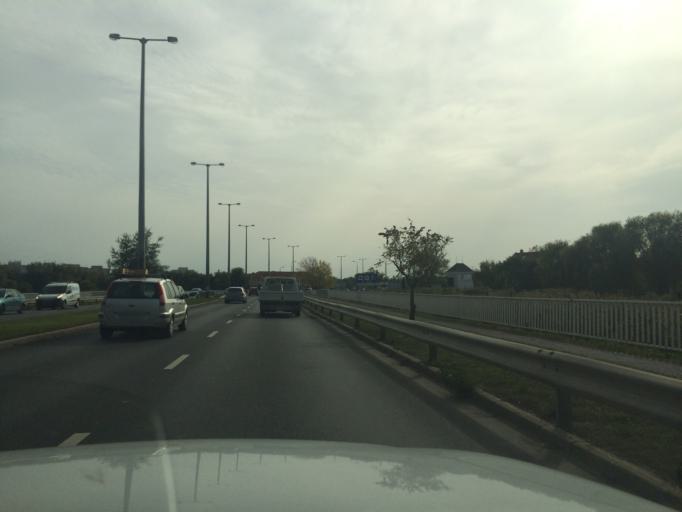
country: HU
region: Szabolcs-Szatmar-Bereg
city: Nyiregyhaza
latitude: 47.9615
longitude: 21.7266
